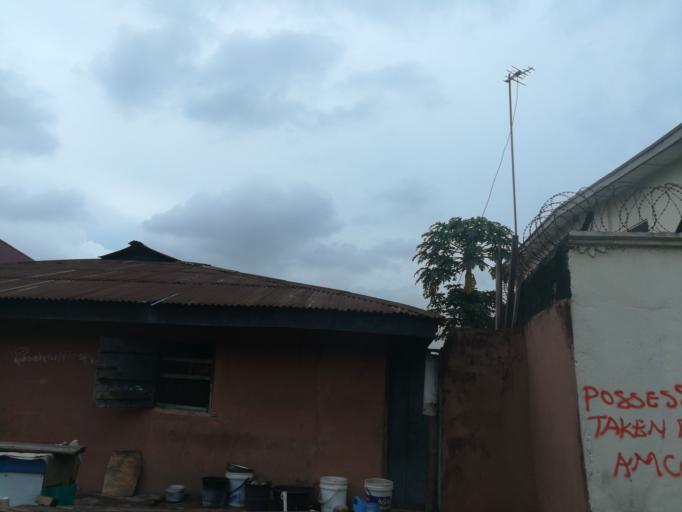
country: NG
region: Lagos
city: Ojota
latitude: 6.5764
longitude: 3.3720
